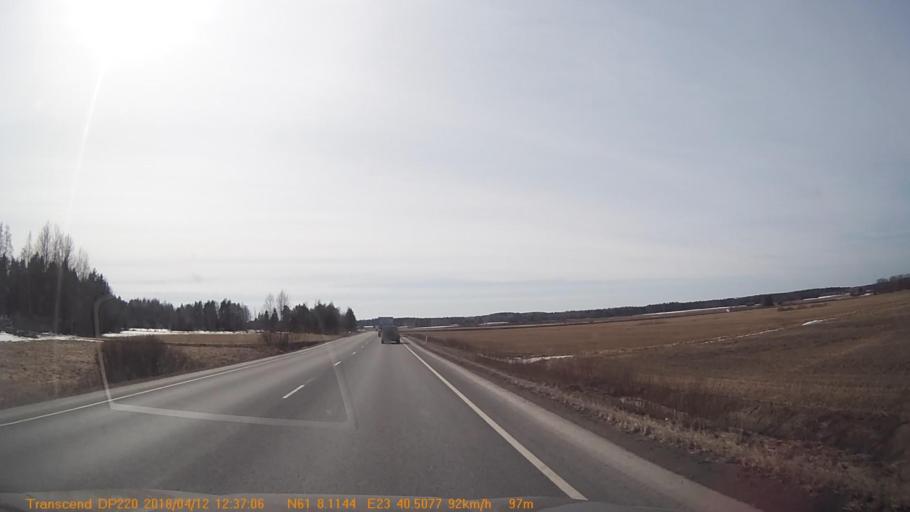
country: FI
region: Pirkanmaa
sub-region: Etelae-Pirkanmaa
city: Kylmaekoski
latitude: 61.1354
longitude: 23.6753
